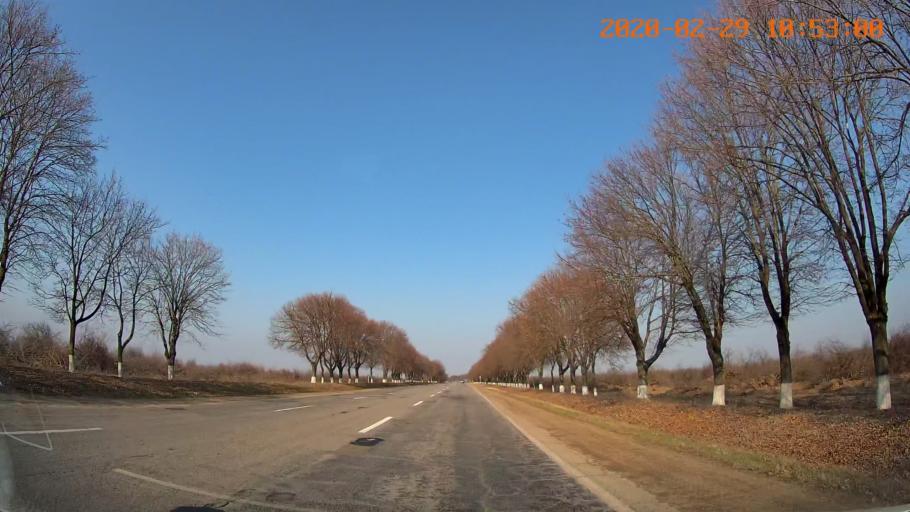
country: MD
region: Telenesti
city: Grigoriopol
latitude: 47.1112
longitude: 29.3422
